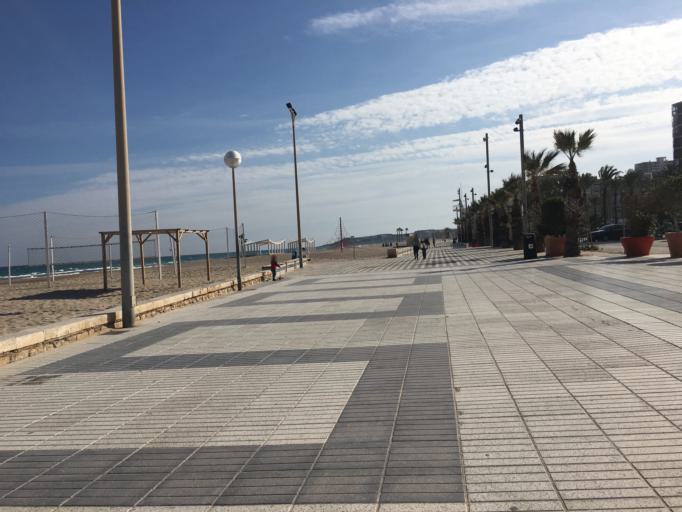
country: ES
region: Valencia
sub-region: Provincia de Alicante
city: San Juan de Alicante
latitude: 38.3758
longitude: -0.4102
